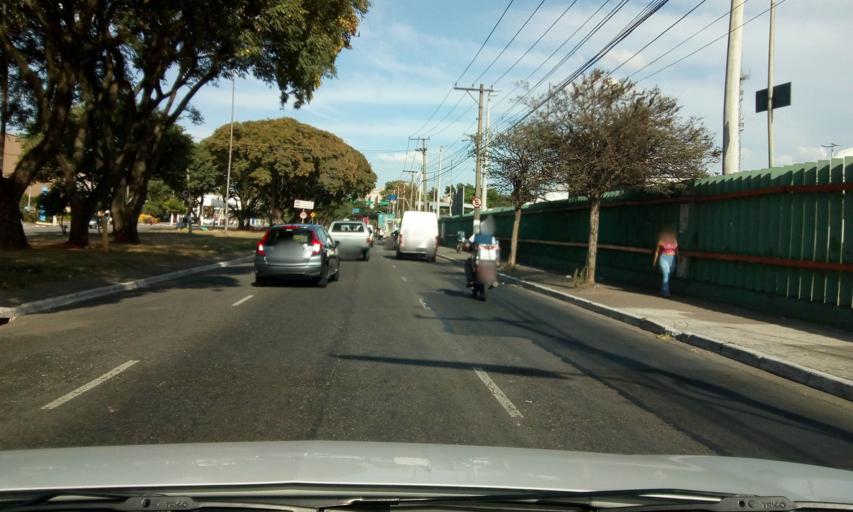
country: BR
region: Sao Paulo
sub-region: Osasco
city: Osasco
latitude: -23.5368
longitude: -46.7323
